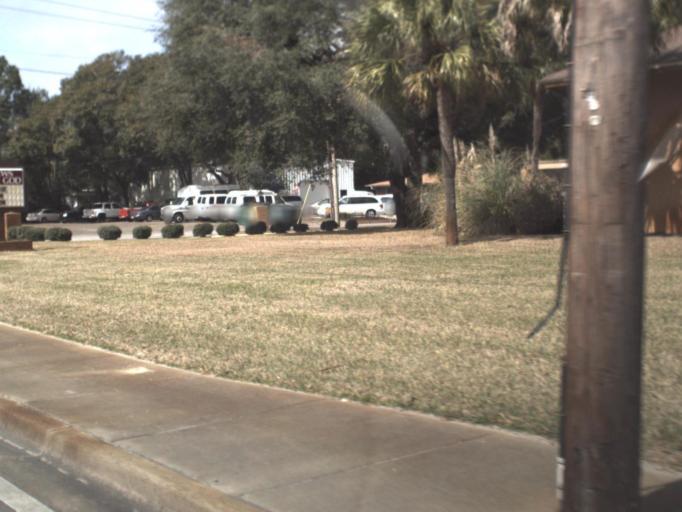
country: US
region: Florida
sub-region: Bay County
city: Pretty Bayou
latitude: 30.1755
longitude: -85.6958
